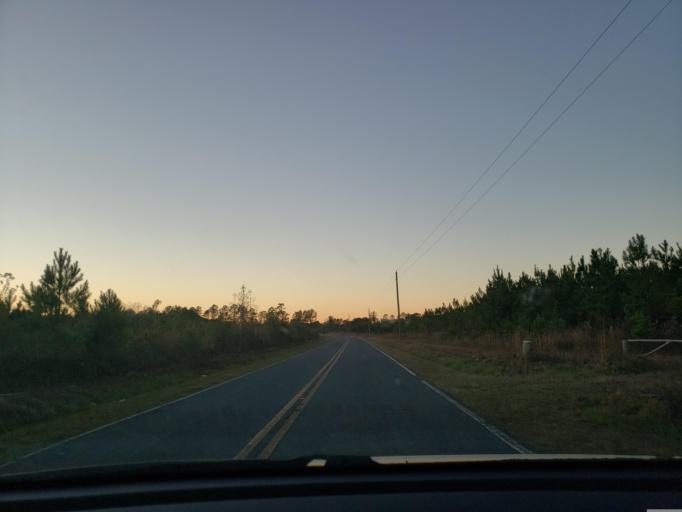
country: US
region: North Carolina
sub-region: Onslow County
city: Richlands
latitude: 34.7375
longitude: -77.6259
